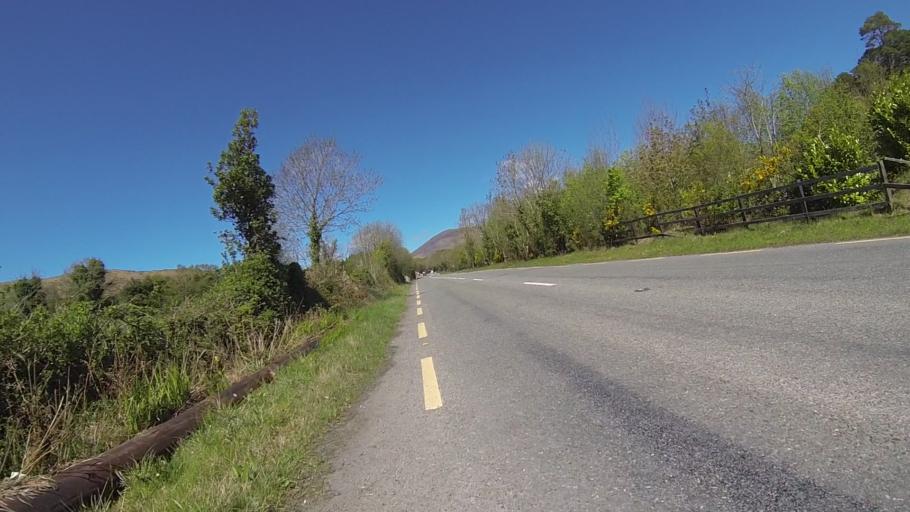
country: IE
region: Munster
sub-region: Ciarrai
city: Kenmare
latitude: 51.8903
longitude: -9.5988
